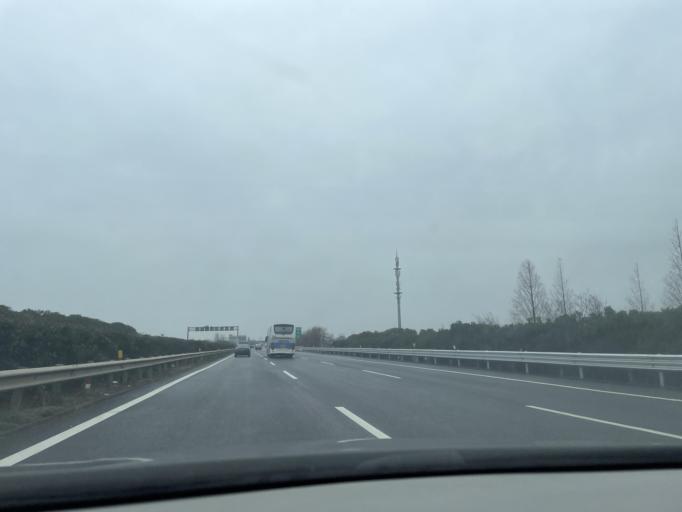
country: CN
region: Zhejiang Sheng
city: Liutangting
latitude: 30.2748
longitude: 121.3051
